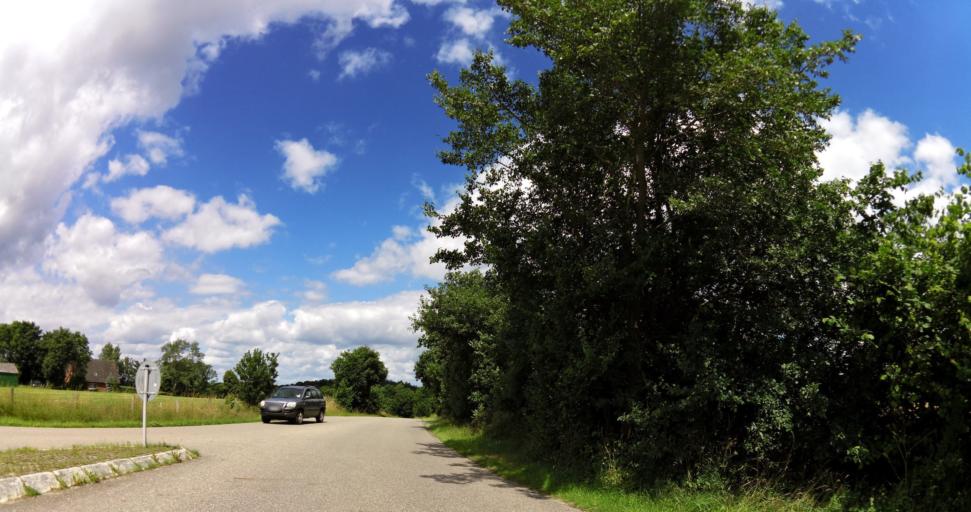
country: DE
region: Schleswig-Holstein
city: Hummelfeld
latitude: 54.4905
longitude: 9.7300
